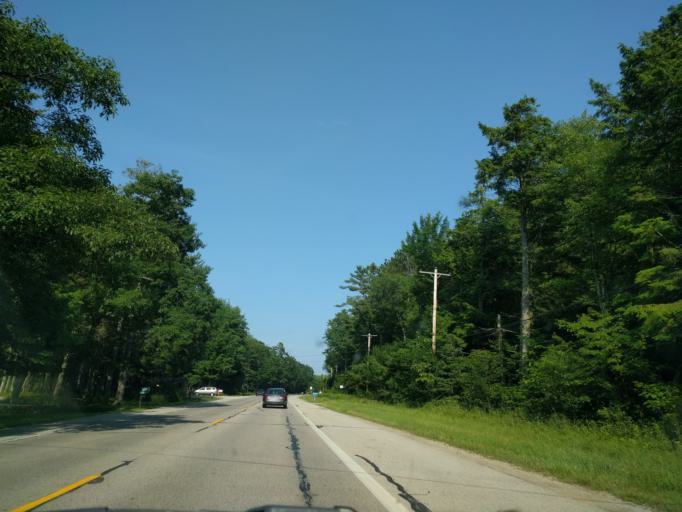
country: US
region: Michigan
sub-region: Delta County
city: Escanaba
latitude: 45.6856
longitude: -87.1202
